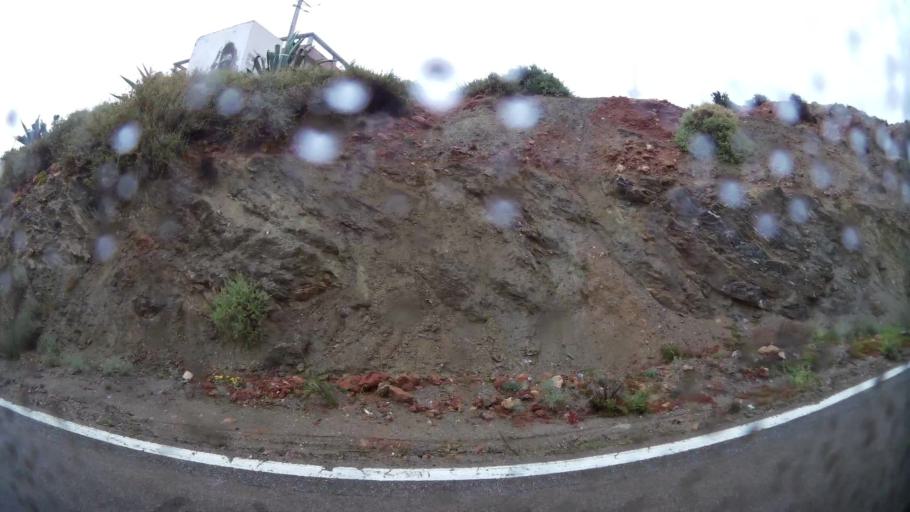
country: MA
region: Taza-Al Hoceima-Taounate
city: Tirhanimine
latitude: 35.2392
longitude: -3.9671
